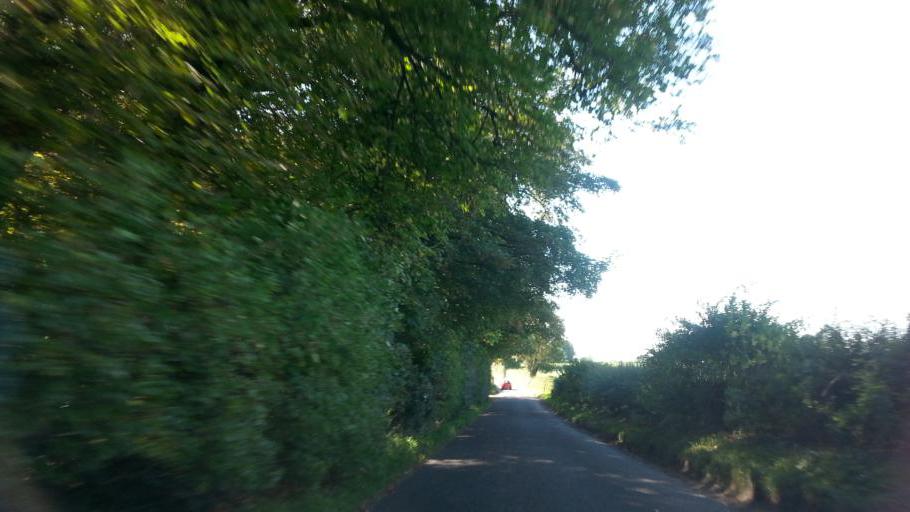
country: GB
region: England
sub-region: Staffordshire
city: Stafford
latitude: 52.8091
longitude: -2.1646
